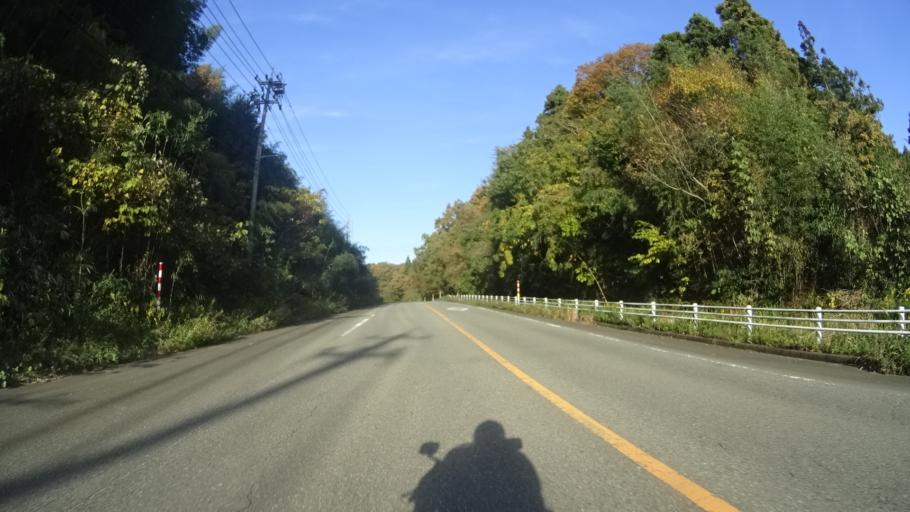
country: JP
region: Ishikawa
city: Hakui
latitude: 37.0499
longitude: 136.7749
